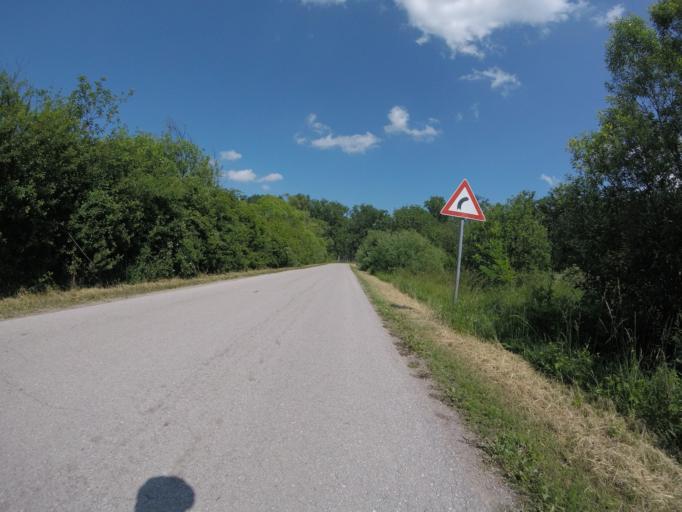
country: HR
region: Zagrebacka
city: Kuce
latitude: 45.6787
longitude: 16.1579
